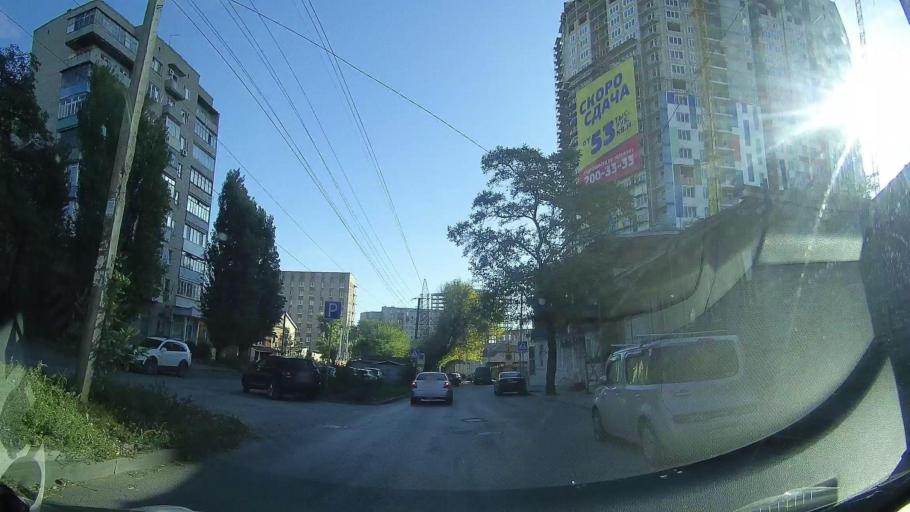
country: RU
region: Rostov
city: Rostov-na-Donu
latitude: 47.2267
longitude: 39.6914
